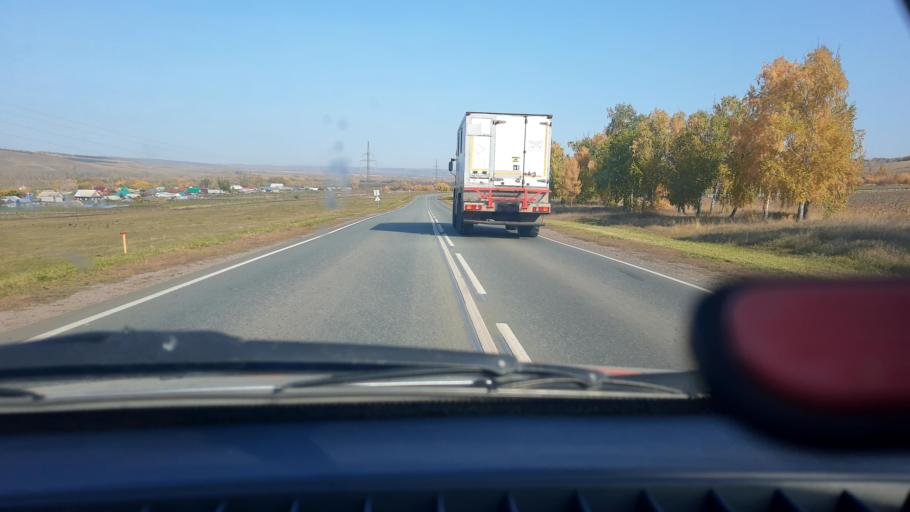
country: RU
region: Bashkortostan
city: Shafranovo
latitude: 53.9639
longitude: 54.7257
